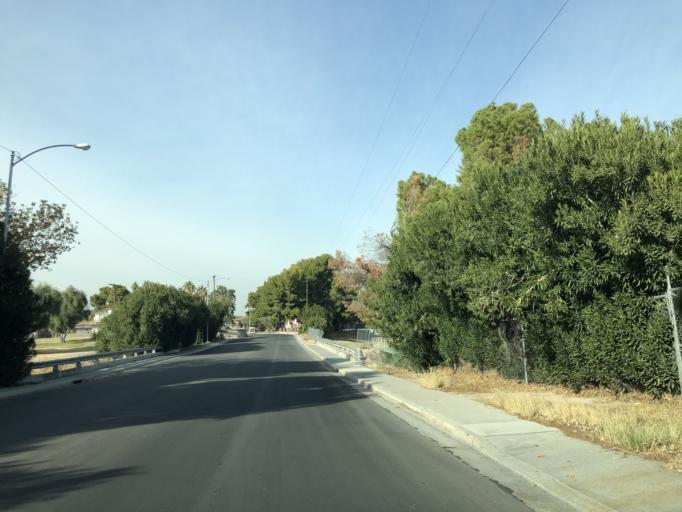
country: US
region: Nevada
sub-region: Clark County
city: Winchester
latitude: 36.1214
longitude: -115.1200
